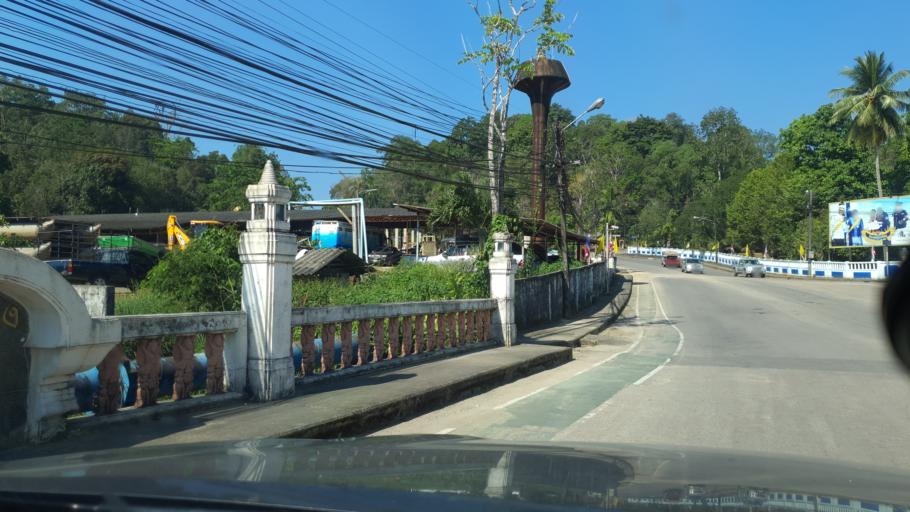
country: TH
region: Ranong
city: Ranong
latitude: 9.9647
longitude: 98.6400
